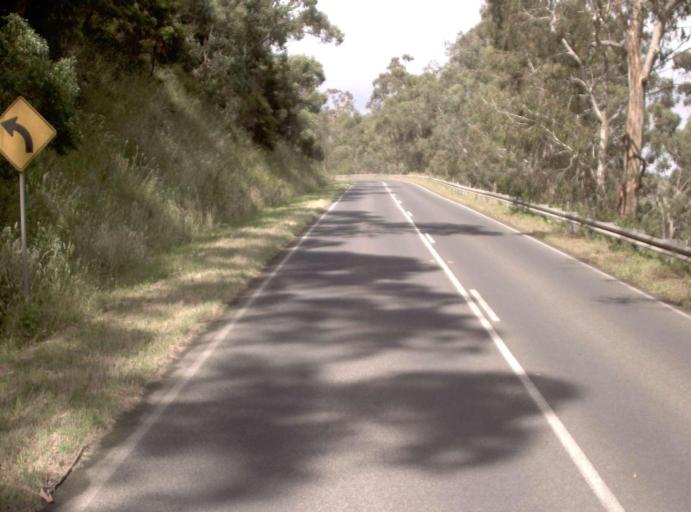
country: AU
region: Victoria
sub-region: Latrobe
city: Morwell
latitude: -38.1720
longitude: 146.3481
